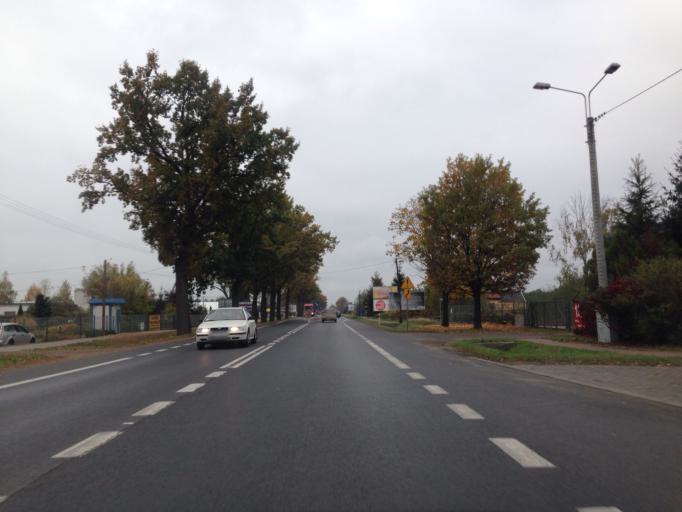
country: PL
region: Kujawsko-Pomorskie
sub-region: Powiat bydgoski
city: Osielsko
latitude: 53.1811
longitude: 18.0637
